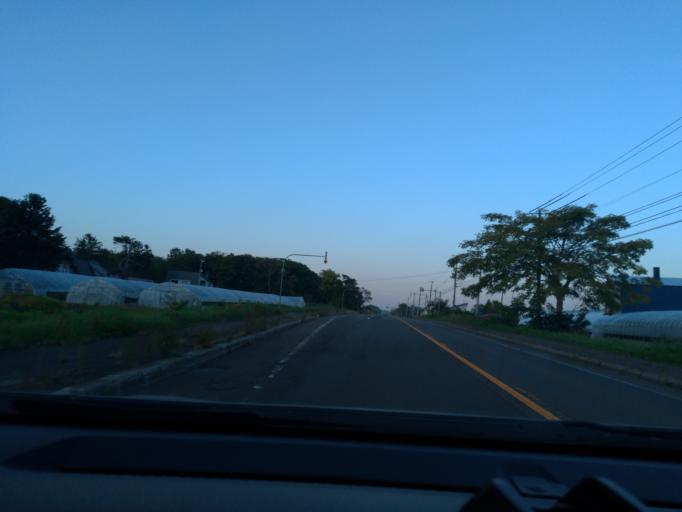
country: JP
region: Hokkaido
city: Tobetsu
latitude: 43.3175
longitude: 141.6046
